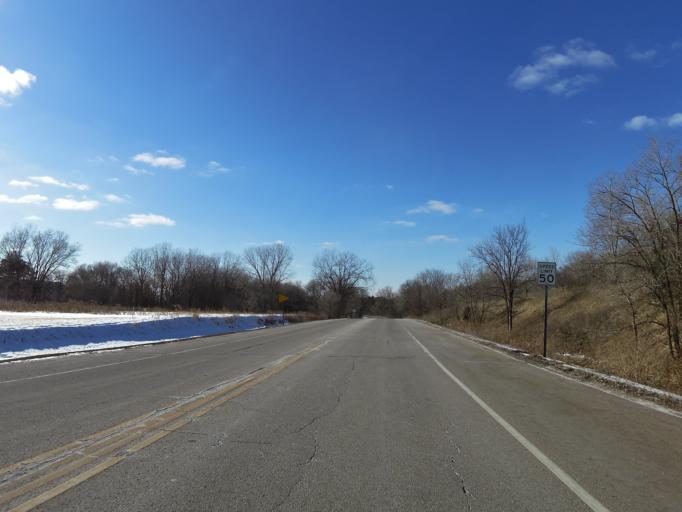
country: US
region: Minnesota
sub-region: Ramsey County
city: Maplewood
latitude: 44.9313
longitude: -92.9924
